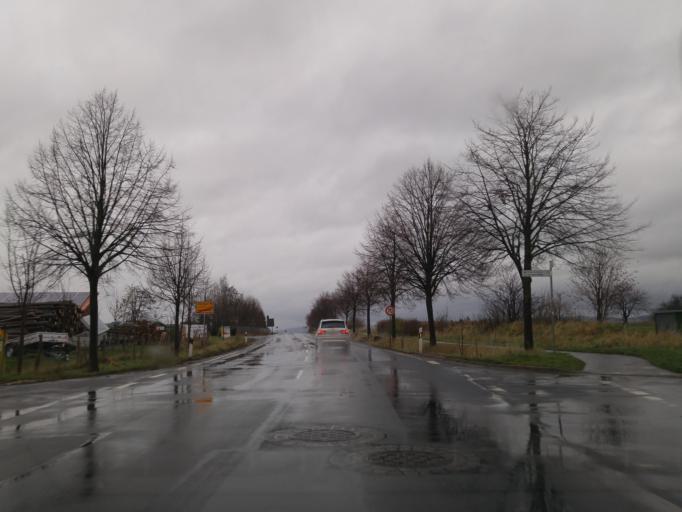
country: DE
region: Lower Saxony
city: Gemeinde Friedland
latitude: 51.4388
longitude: 9.9298
